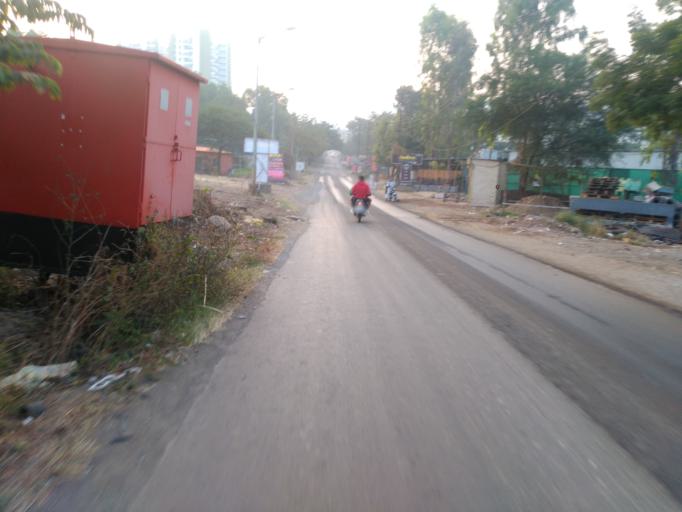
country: IN
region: Maharashtra
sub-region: Pune Division
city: Pune
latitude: 18.4296
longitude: 73.8987
